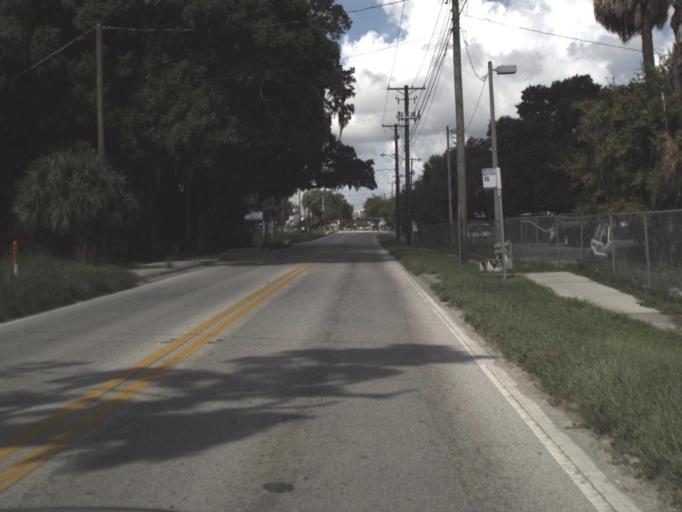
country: US
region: Florida
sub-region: Hillsborough County
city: East Lake-Orient Park
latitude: 27.9628
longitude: -82.3980
